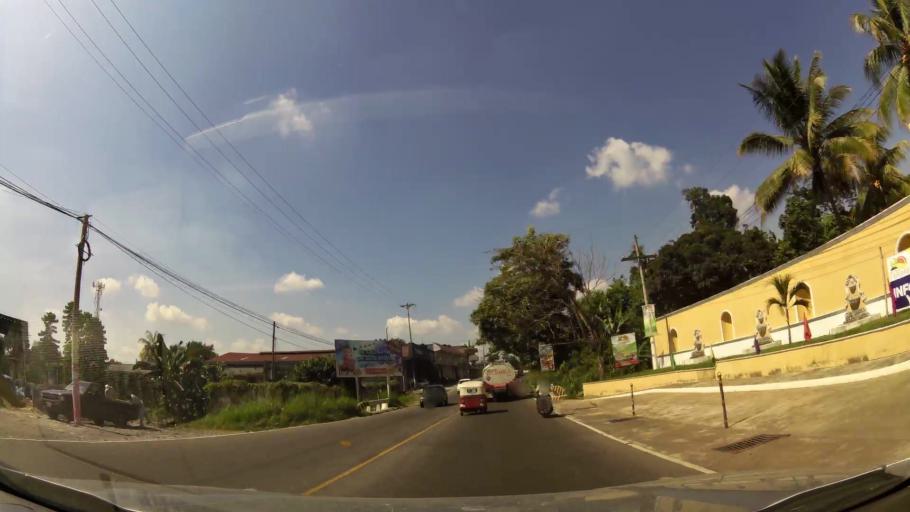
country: GT
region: Suchitepeque
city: Mazatenango
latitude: 14.5323
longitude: -91.4833
